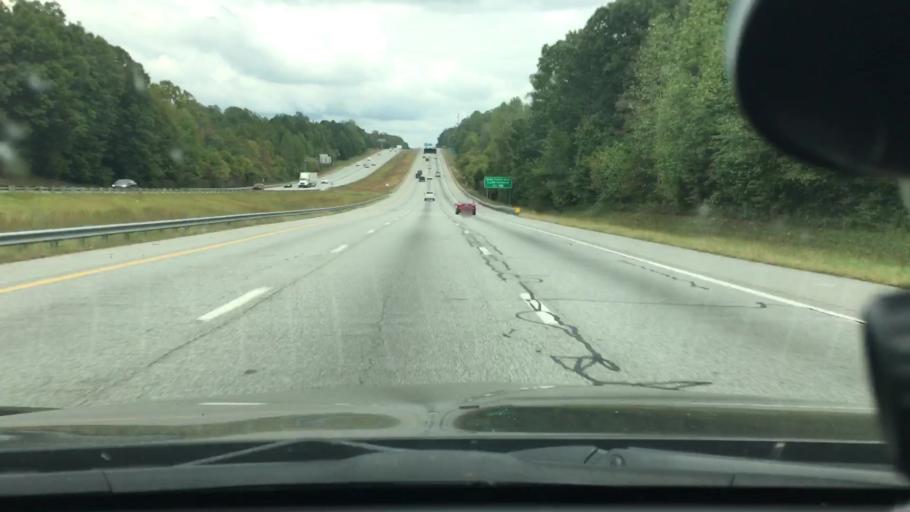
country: US
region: North Carolina
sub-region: Forsyth County
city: Clemmons
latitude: 36.0533
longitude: -80.3562
